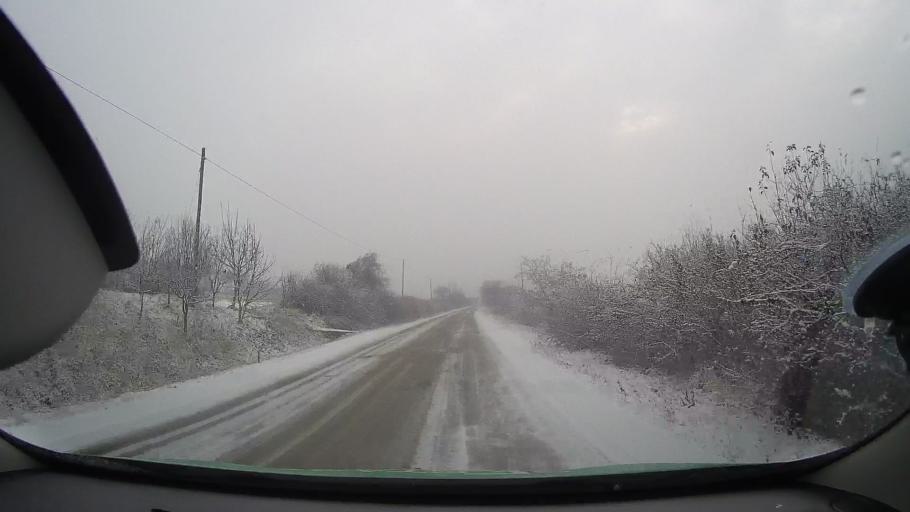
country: RO
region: Alba
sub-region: Municipiul Aiud
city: Aiudul de Sus
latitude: 46.3311
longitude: 23.6750
